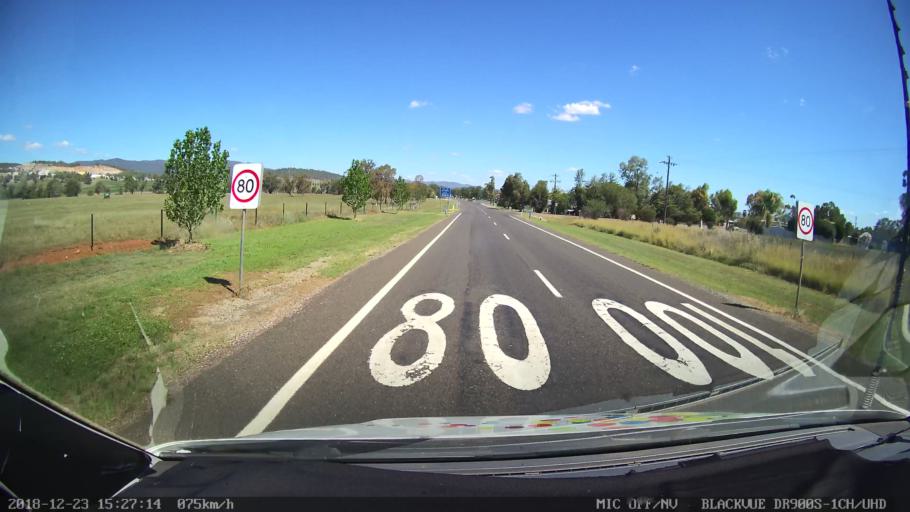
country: AU
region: New South Wales
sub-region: Tamworth Municipality
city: East Tamworth
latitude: -30.9258
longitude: 150.8441
